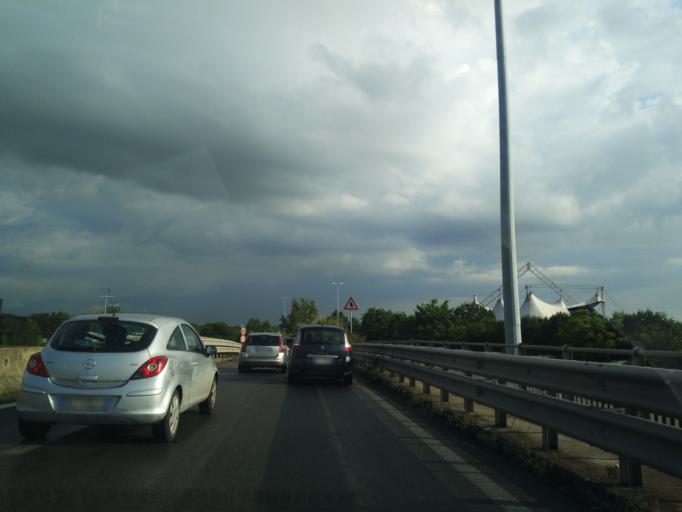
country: IT
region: Latium
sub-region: Citta metropolitana di Roma Capitale
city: Rome
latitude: 41.9030
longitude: 12.5738
